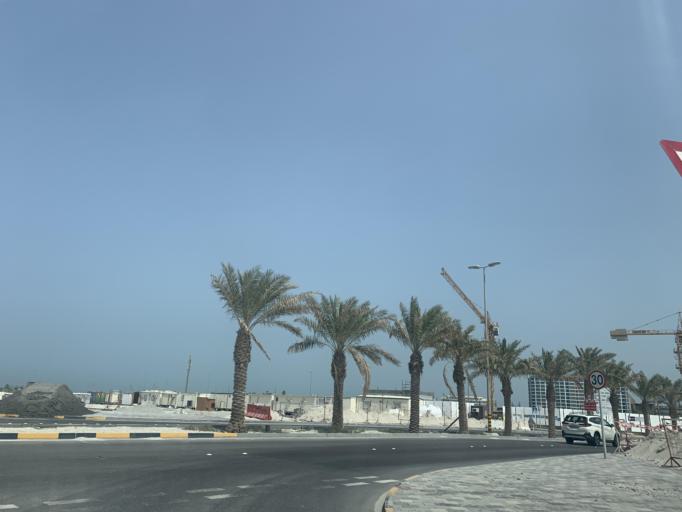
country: BH
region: Muharraq
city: Al Hadd
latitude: 26.2734
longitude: 50.6728
